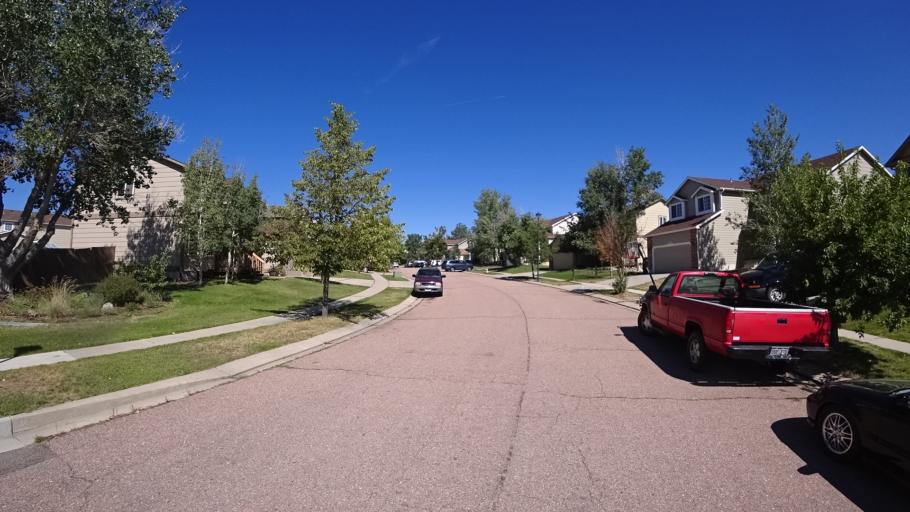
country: US
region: Colorado
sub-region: El Paso County
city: Black Forest
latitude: 38.9532
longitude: -104.7294
